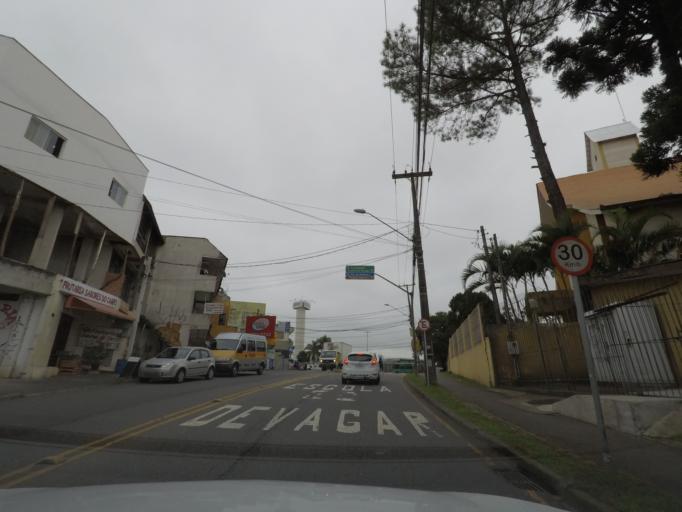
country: BR
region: Parana
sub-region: Curitiba
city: Curitiba
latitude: -25.4612
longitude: -49.3443
